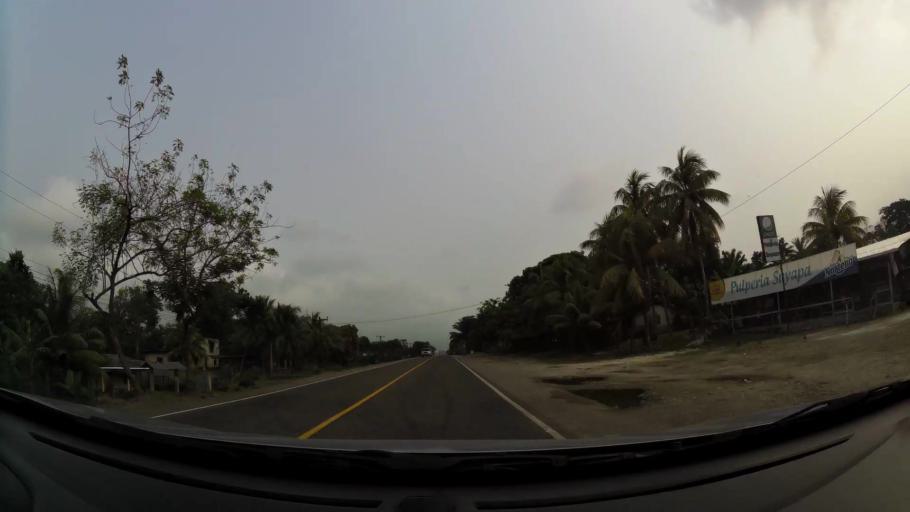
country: HN
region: Atlantida
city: Mezapa
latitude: 15.6078
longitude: -87.6124
